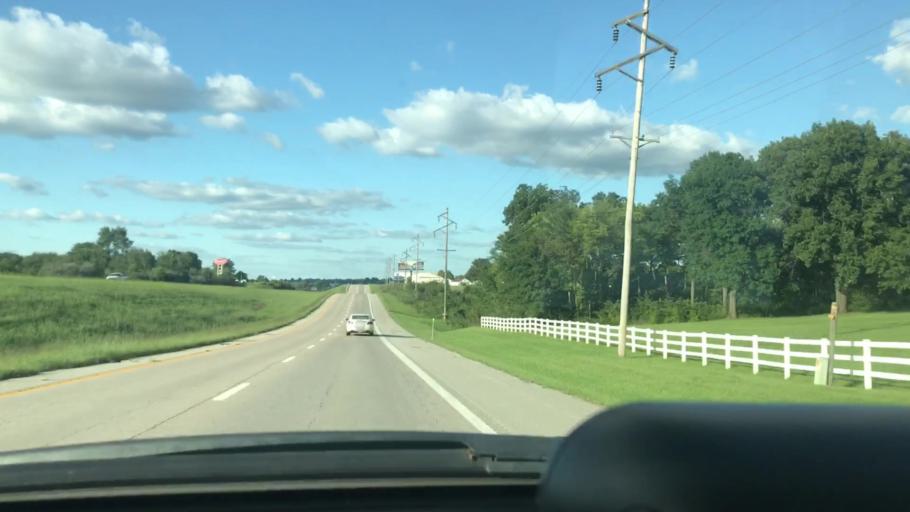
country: US
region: Missouri
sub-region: Pettis County
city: Sedalia
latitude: 38.6467
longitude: -93.2609
